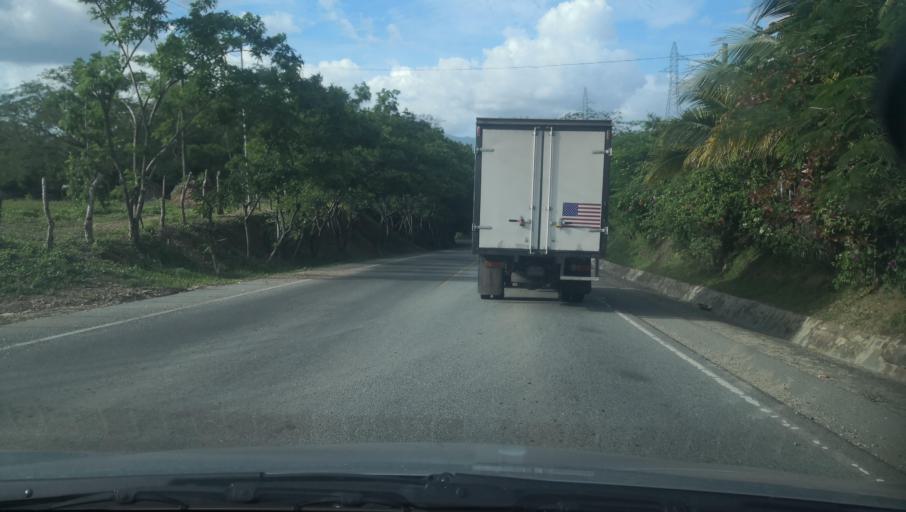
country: NI
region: Nueva Segovia
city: Ocotal
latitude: 13.6060
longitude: -86.4710
